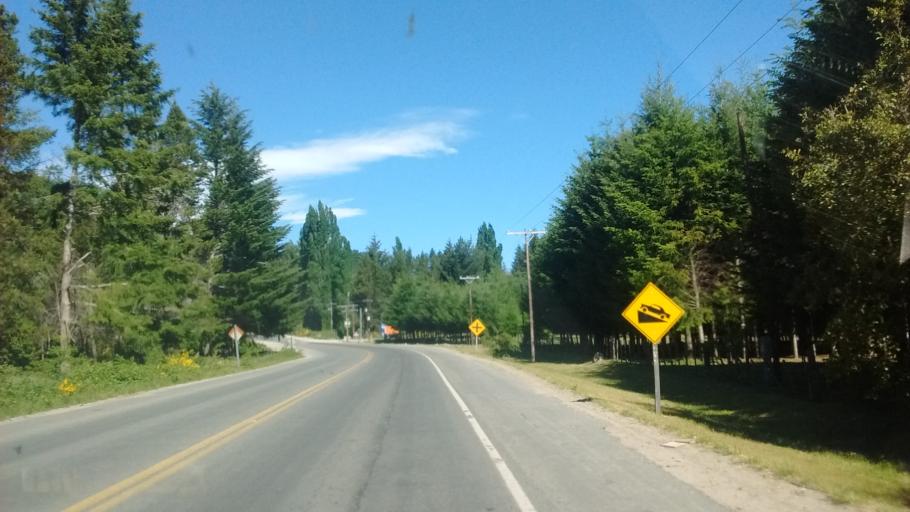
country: AR
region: Chubut
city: Hoyo de Epuyen
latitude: -42.0341
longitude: -71.5647
